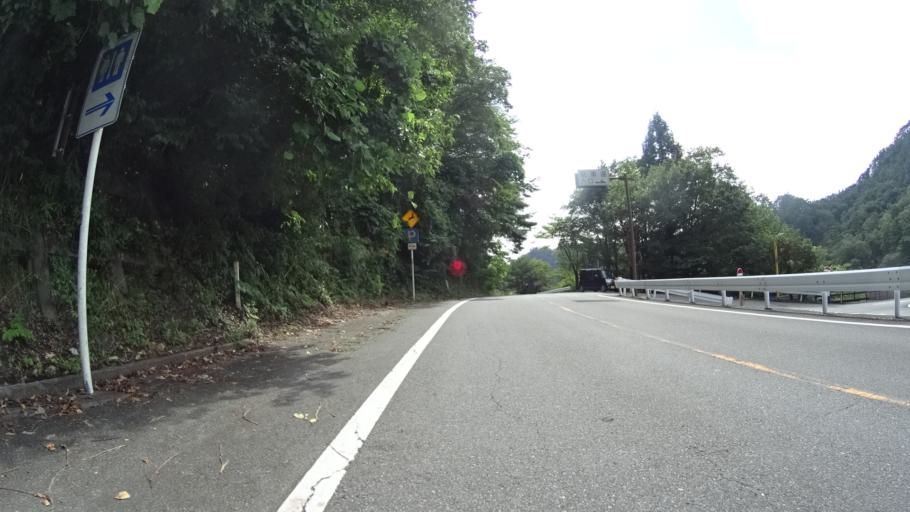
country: JP
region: Yamanashi
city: Kofu-shi
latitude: 35.7380
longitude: 138.5654
